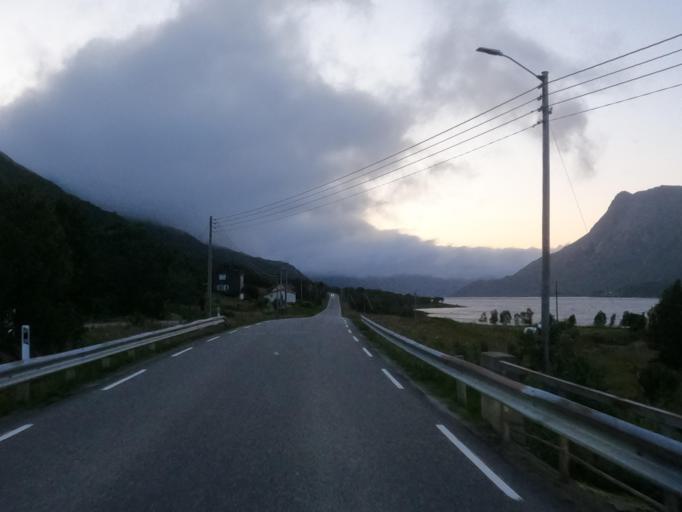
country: NO
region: Nordland
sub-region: Lodingen
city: Lodingen
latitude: 68.5709
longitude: 15.7960
